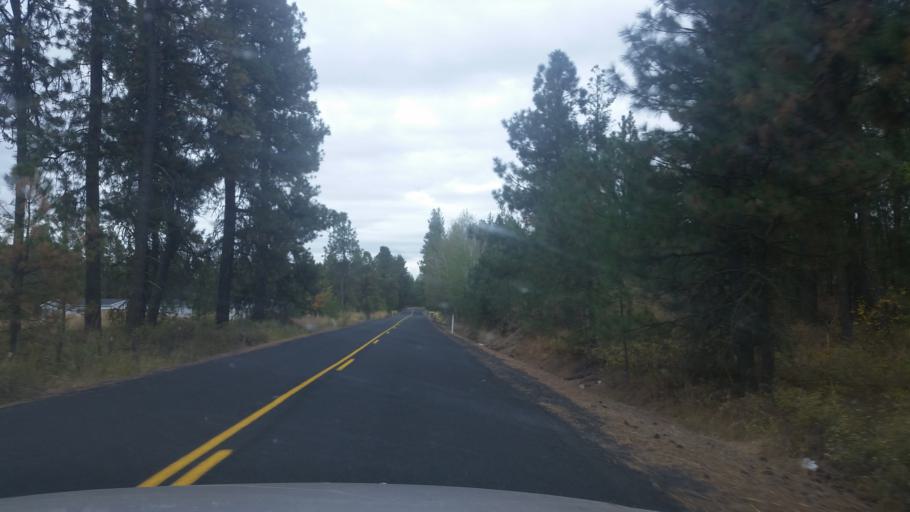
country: US
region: Washington
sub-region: Spokane County
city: Medical Lake
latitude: 47.4988
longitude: -117.7717
